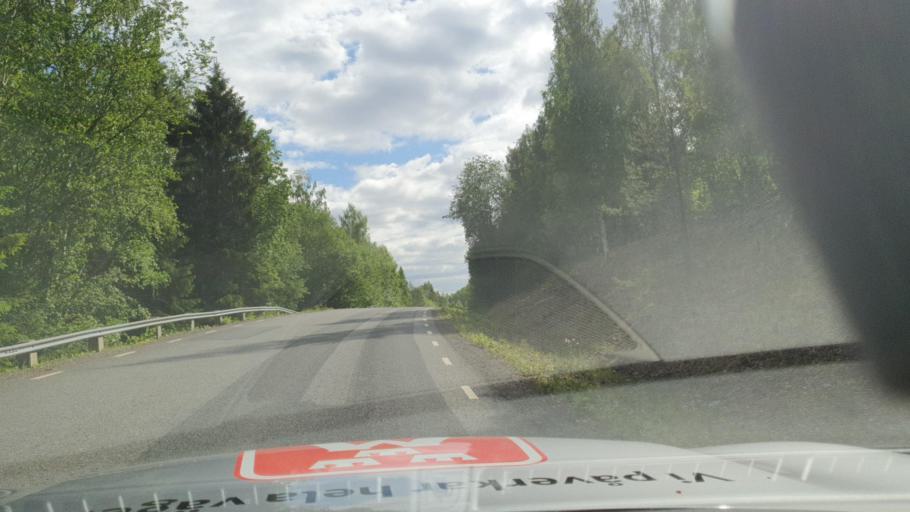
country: SE
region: Vaesternorrland
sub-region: Kramfors Kommun
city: Nordingra
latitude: 62.8225
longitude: 18.1778
